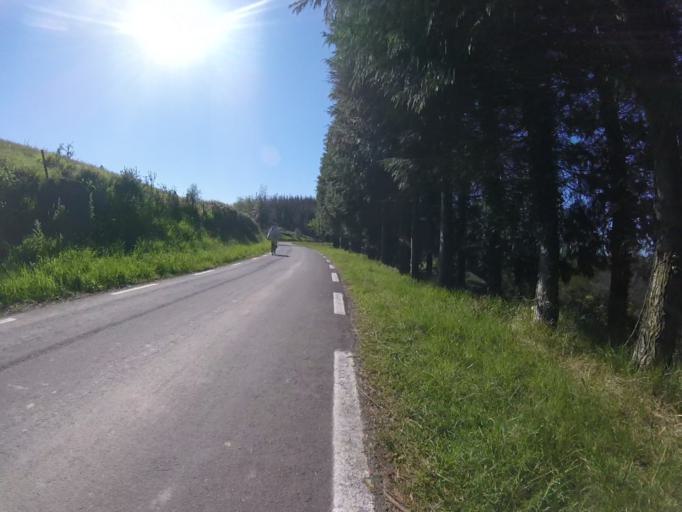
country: ES
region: Basque Country
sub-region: Provincia de Guipuzcoa
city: Aizarnazabal
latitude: 43.2127
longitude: -2.2026
